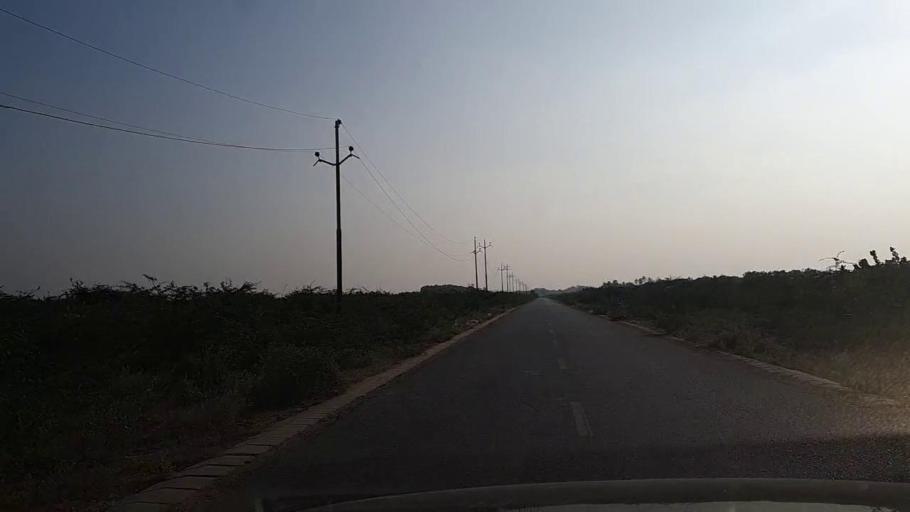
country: PK
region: Sindh
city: Gharo
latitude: 24.7906
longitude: 67.5158
